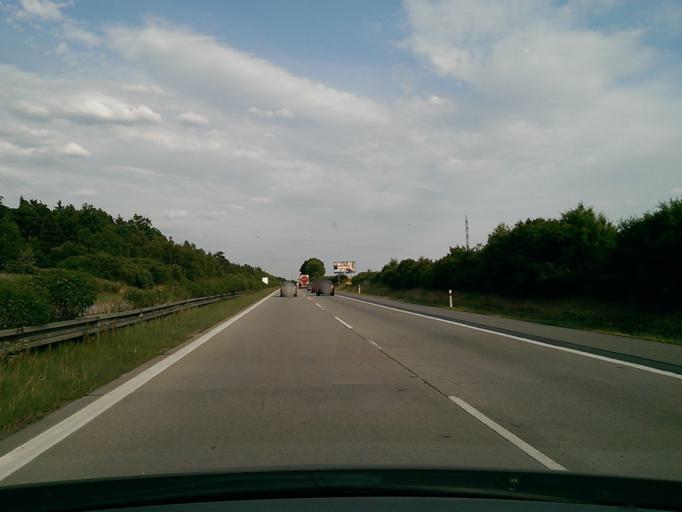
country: CZ
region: Vysocina
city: Dobronin
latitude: 49.4454
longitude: 15.6246
